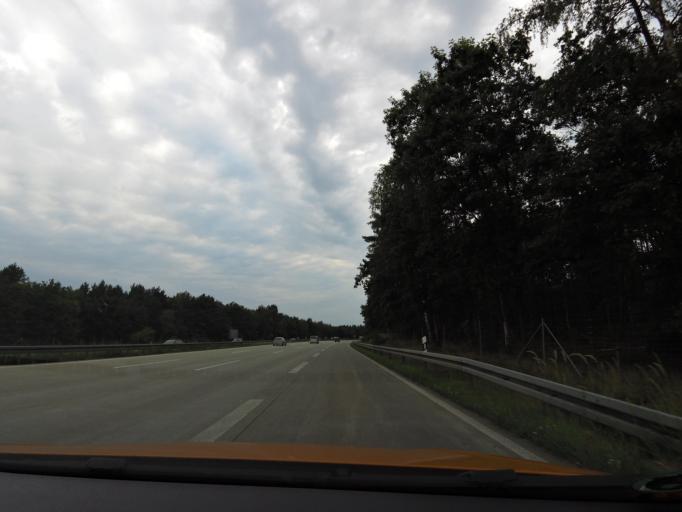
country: DE
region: Berlin
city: Wannsee
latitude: 52.3864
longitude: 13.1541
